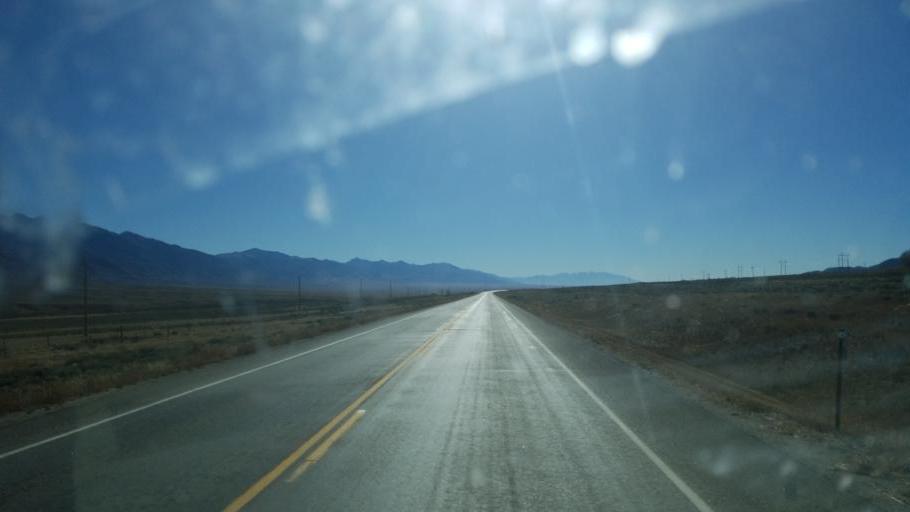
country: US
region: Colorado
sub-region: Chaffee County
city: Salida
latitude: 38.3752
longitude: -106.0441
